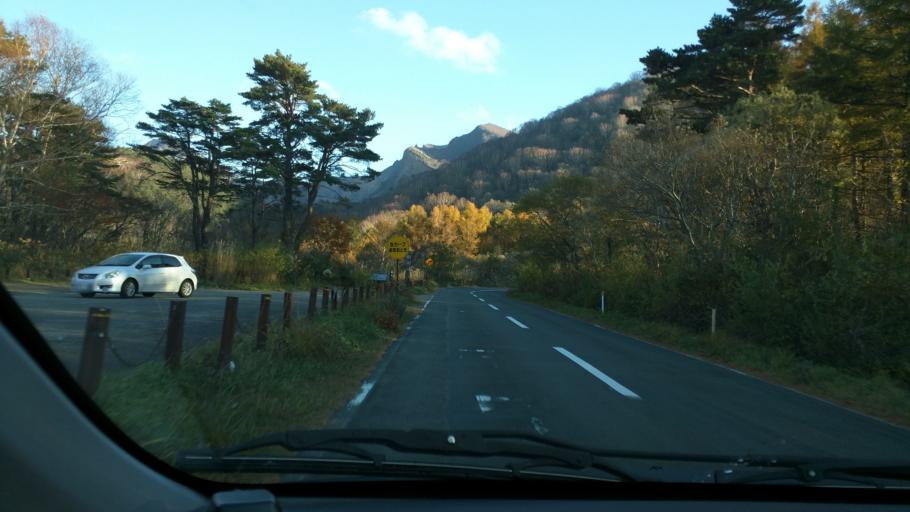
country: JP
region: Fukushima
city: Inawashiro
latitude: 37.6227
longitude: 140.0542
